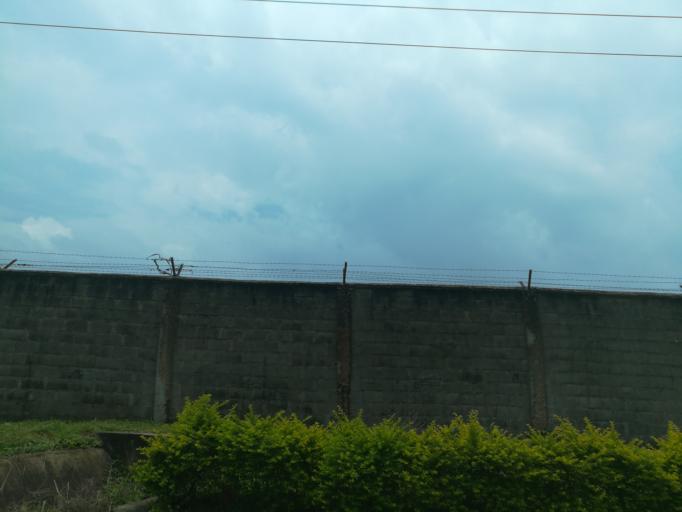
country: NG
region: Lagos
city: Ikorodu
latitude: 6.5635
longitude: 3.6025
